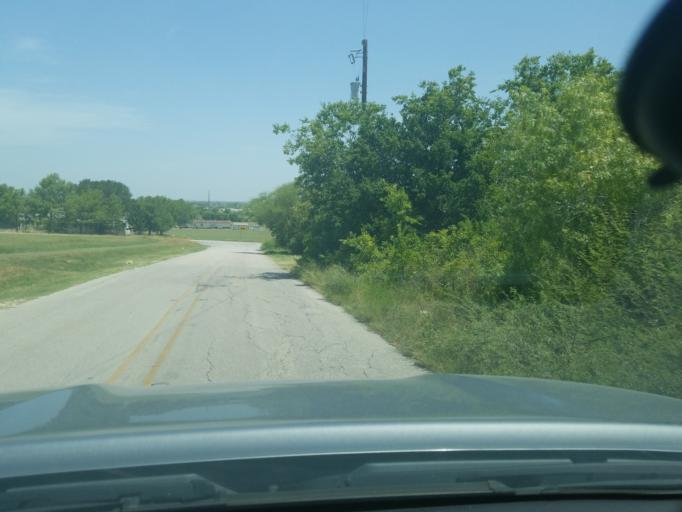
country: US
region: Texas
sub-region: Guadalupe County
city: Cibolo
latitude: 29.5835
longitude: -98.2105
